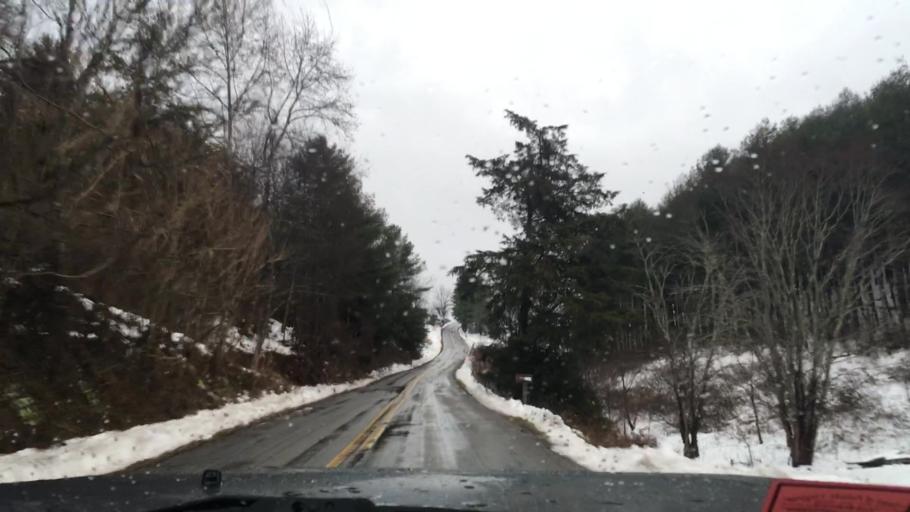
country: US
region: Virginia
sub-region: Pulaski County
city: Dublin
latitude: 37.0080
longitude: -80.6624
